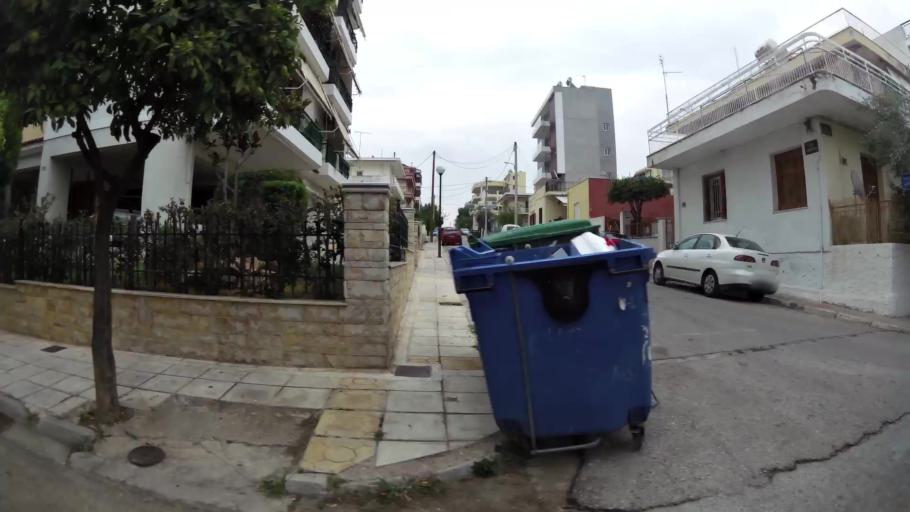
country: GR
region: Attica
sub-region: Nomarchia Athinas
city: Ilion
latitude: 38.0359
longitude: 23.7051
